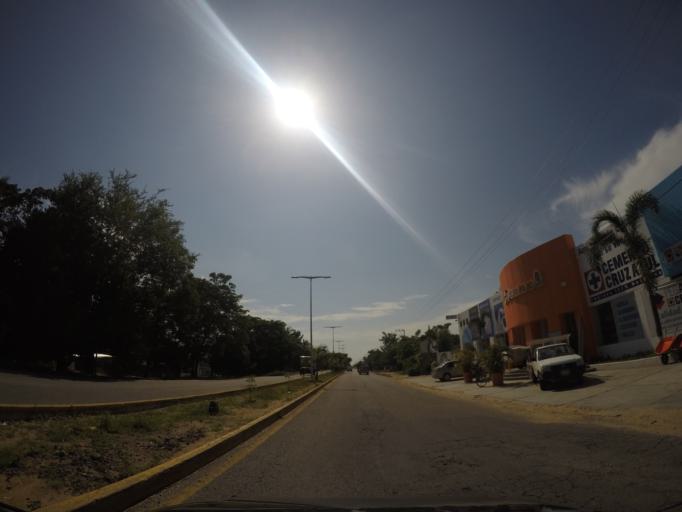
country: MX
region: Oaxaca
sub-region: San Pedro Mixtepec -Dto. 22 -
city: Puerto Escondido
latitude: 15.8688
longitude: -97.0831
